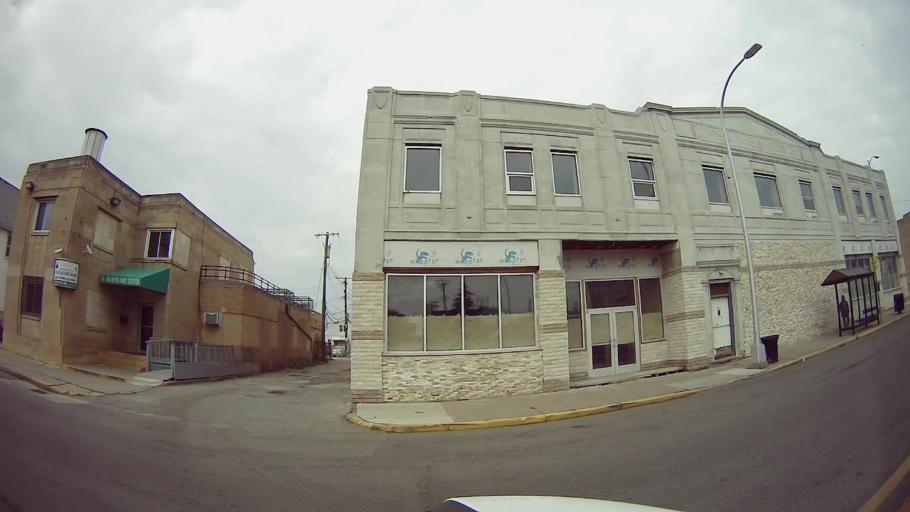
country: US
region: Michigan
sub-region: Wayne County
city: Hamtramck
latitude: 42.3996
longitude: -83.0604
